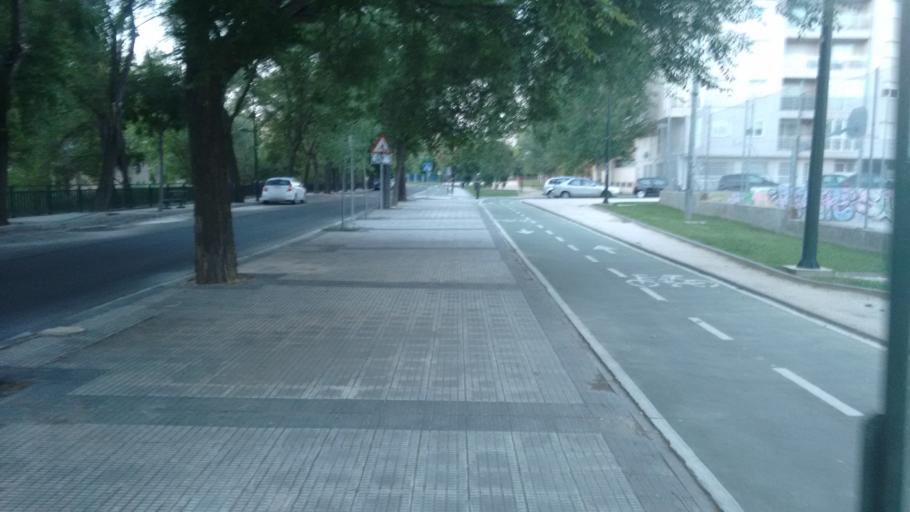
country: ES
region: Aragon
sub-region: Provincia de Zaragoza
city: Zaragoza
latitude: 41.6324
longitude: -0.8821
